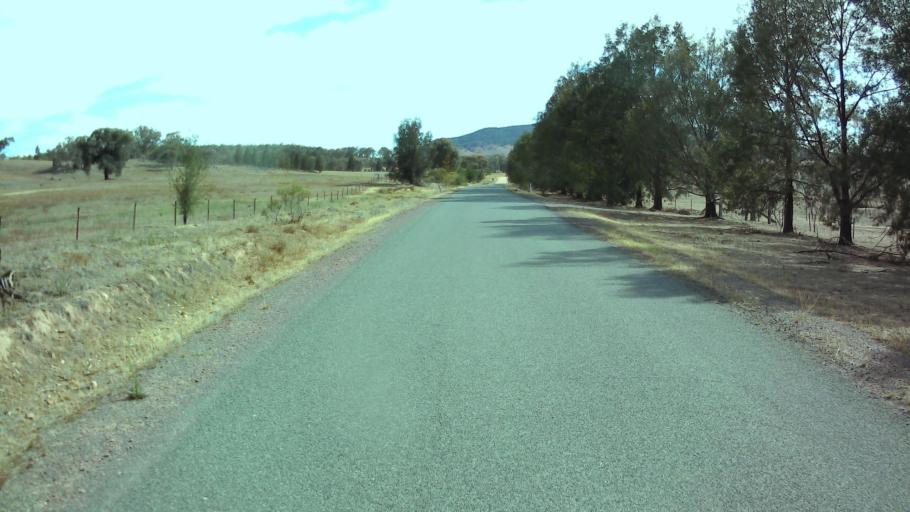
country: AU
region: New South Wales
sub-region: Weddin
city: Grenfell
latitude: -33.8105
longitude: 148.2929
